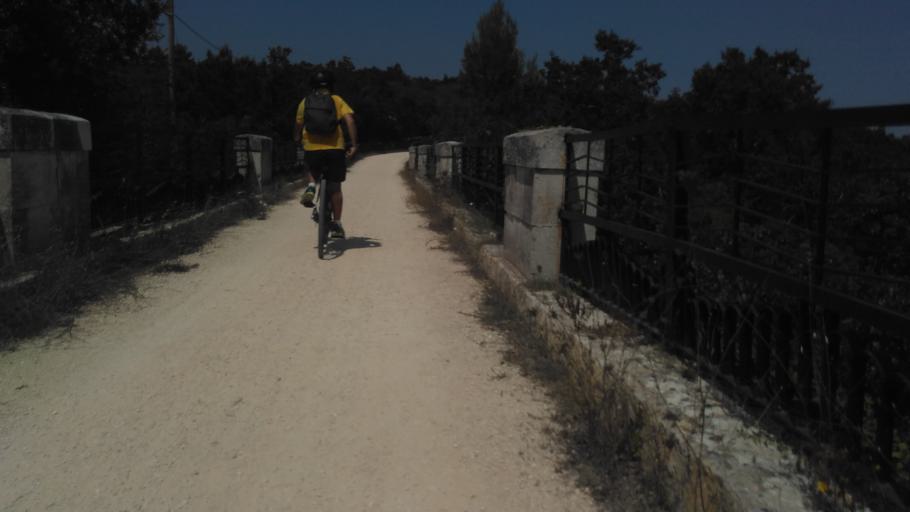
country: IT
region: Apulia
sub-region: Provincia di Brindisi
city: Cisternino
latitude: 40.6802
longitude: 17.4311
